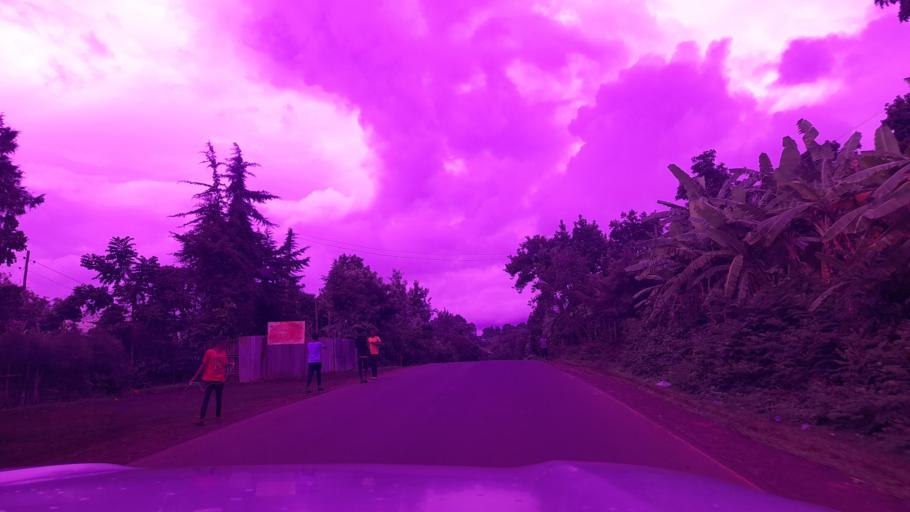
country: ET
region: Oromiya
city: Jima
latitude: 7.9053
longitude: 37.3913
